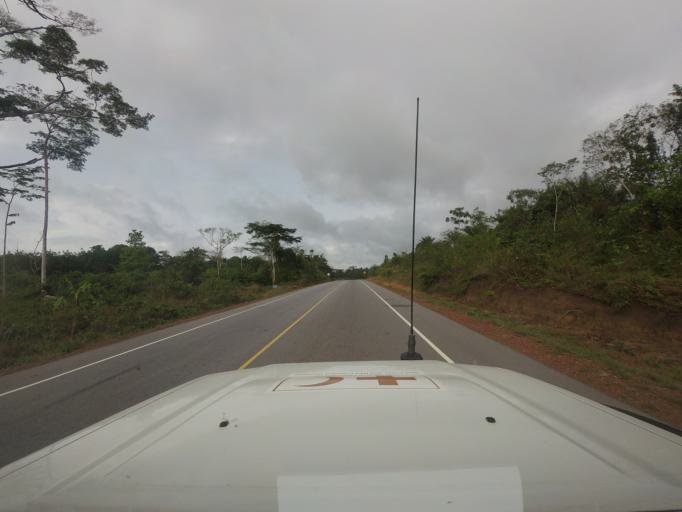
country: LR
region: Bong
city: Gbarnga
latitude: 7.0374
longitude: -9.2641
